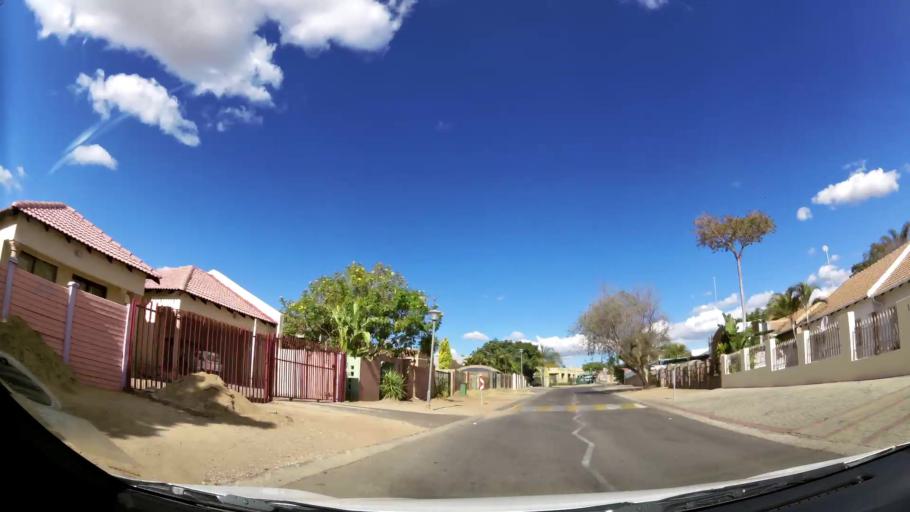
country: ZA
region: Limpopo
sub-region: Capricorn District Municipality
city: Polokwane
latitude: -23.8824
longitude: 29.4716
